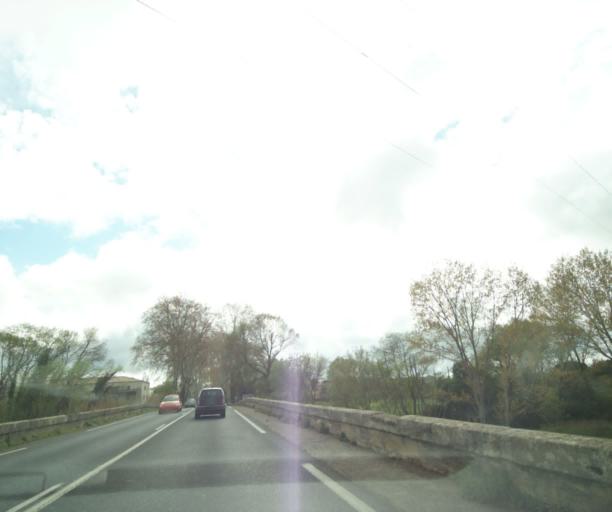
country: FR
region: Languedoc-Roussillon
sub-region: Departement de l'Herault
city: Fabregues
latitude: 43.5528
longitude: 3.7861
